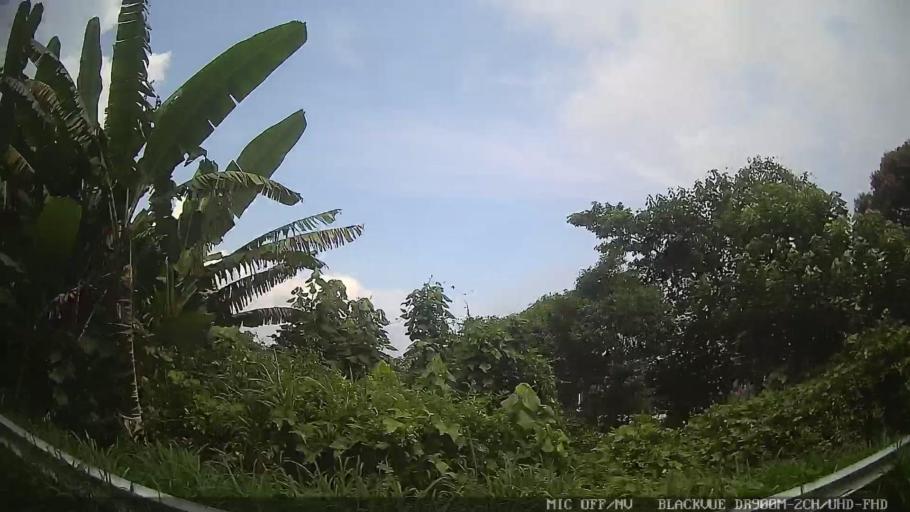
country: BR
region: Sao Paulo
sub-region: Ribeirao Pires
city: Ribeirao Pires
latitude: -23.6893
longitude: -46.3880
